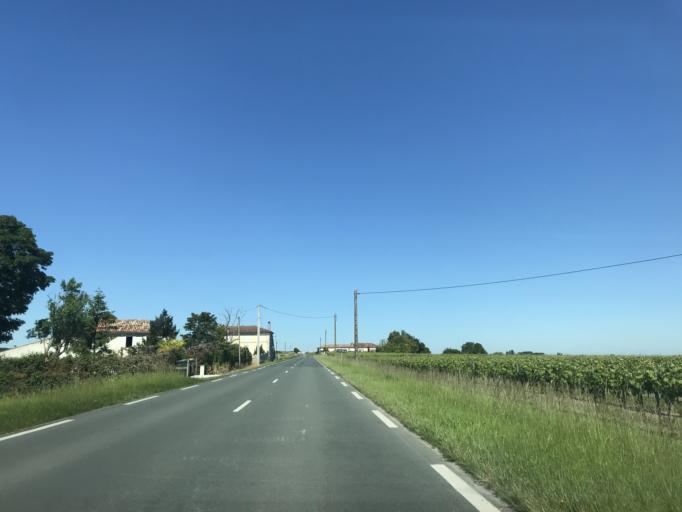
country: FR
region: Poitou-Charentes
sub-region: Departement de la Charente
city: Chateaubernard
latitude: 45.5350
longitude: -0.3233
